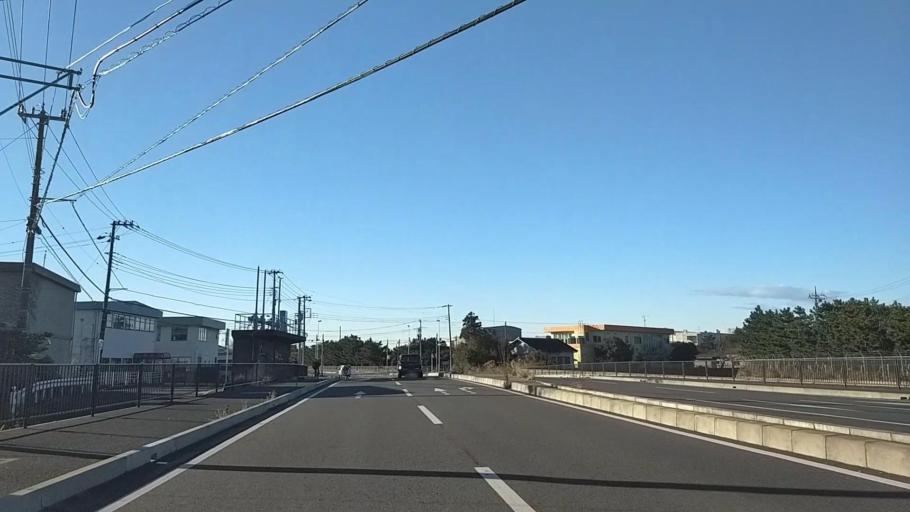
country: JP
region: Chiba
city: Kisarazu
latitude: 35.3937
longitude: 139.9197
